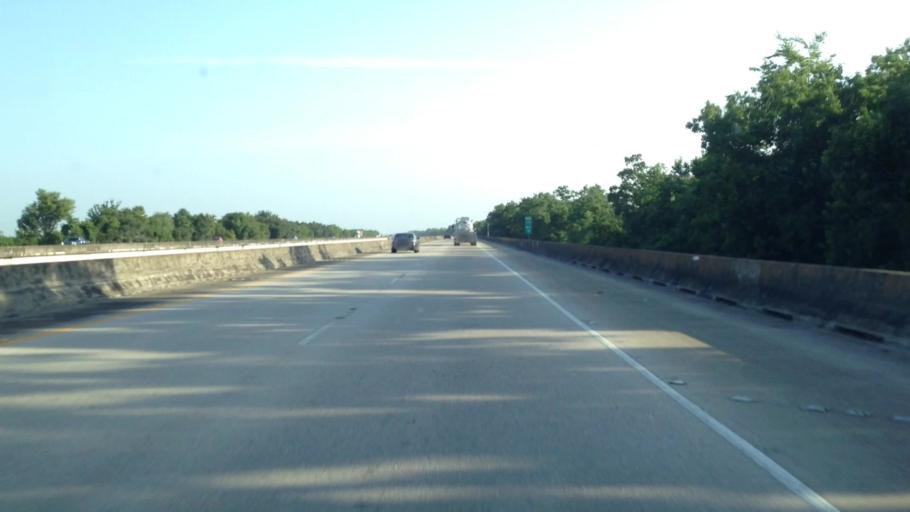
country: US
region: Louisiana
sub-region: Tangipahoa Parish
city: Ponchatoula
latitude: 30.3322
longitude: -90.4109
